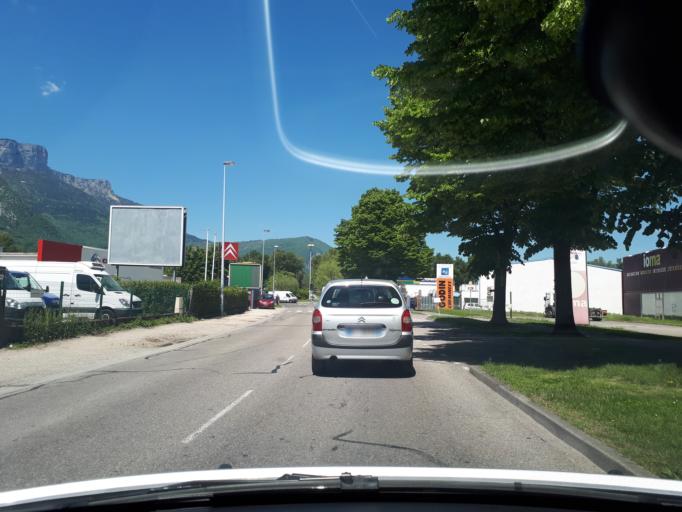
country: FR
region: Rhone-Alpes
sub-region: Departement de l'Isere
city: Saint-Egreve
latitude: 45.2229
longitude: 5.6749
